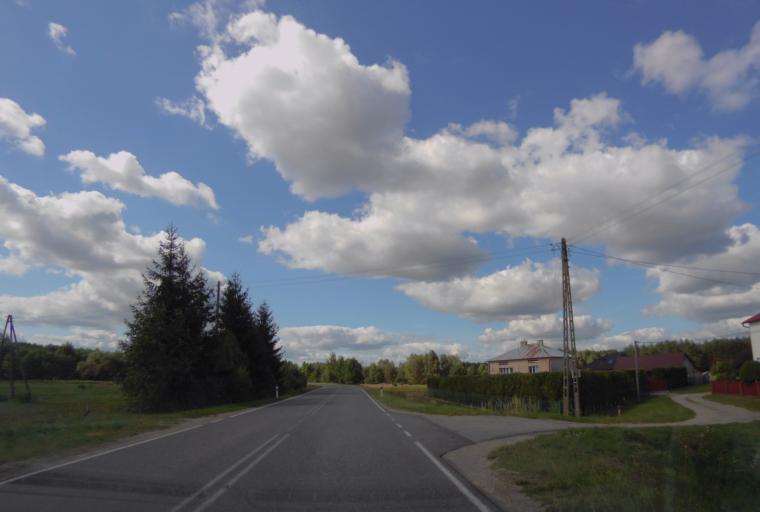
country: PL
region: Subcarpathian Voivodeship
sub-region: Powiat tarnobrzeski
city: Nowa Deba
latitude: 50.4080
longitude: 21.8162
